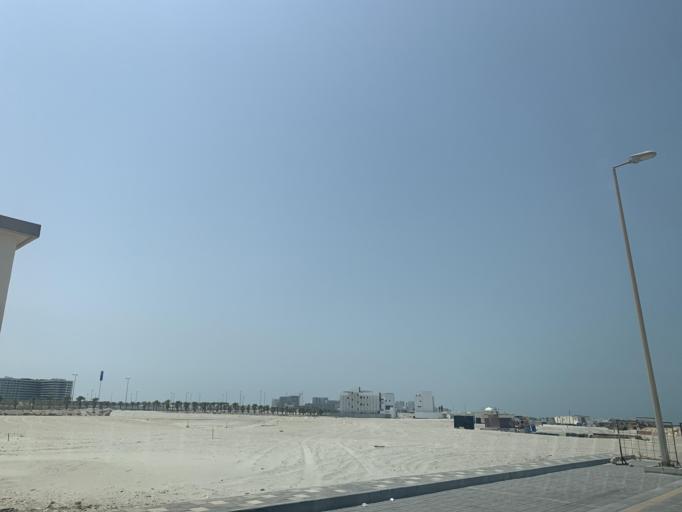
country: BH
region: Muharraq
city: Al Hadd
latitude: 26.2722
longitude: 50.6810
